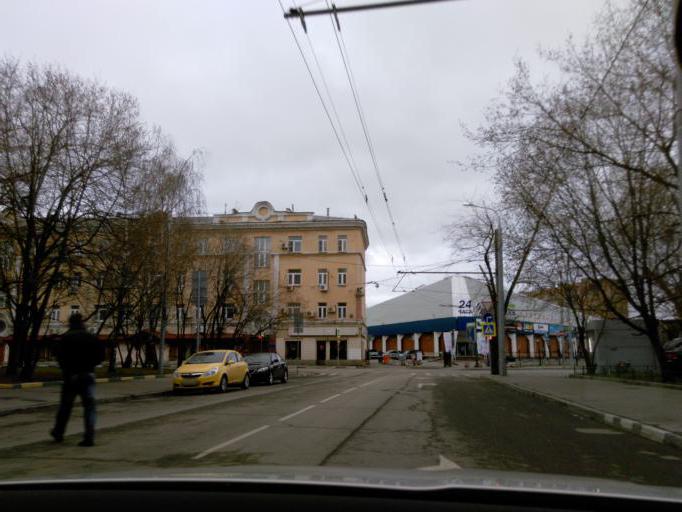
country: RU
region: Moskovskaya
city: Dorogomilovo
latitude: 55.7702
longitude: 37.5853
